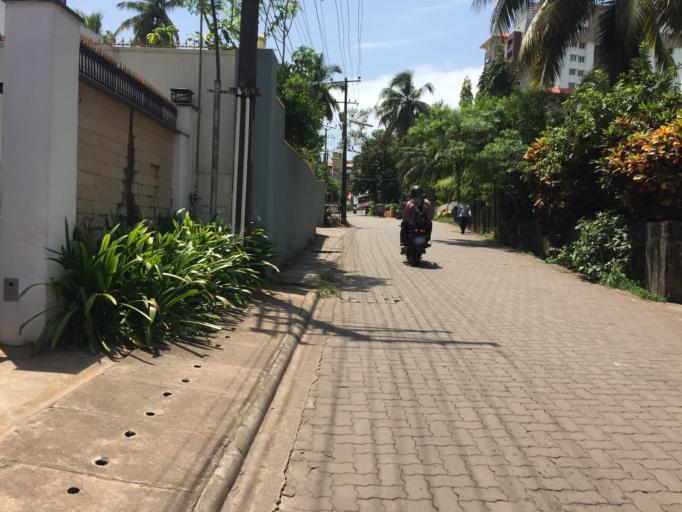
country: IN
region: Karnataka
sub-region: Dakshina Kannada
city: Mangalore
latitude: 12.8782
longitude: 74.8515
